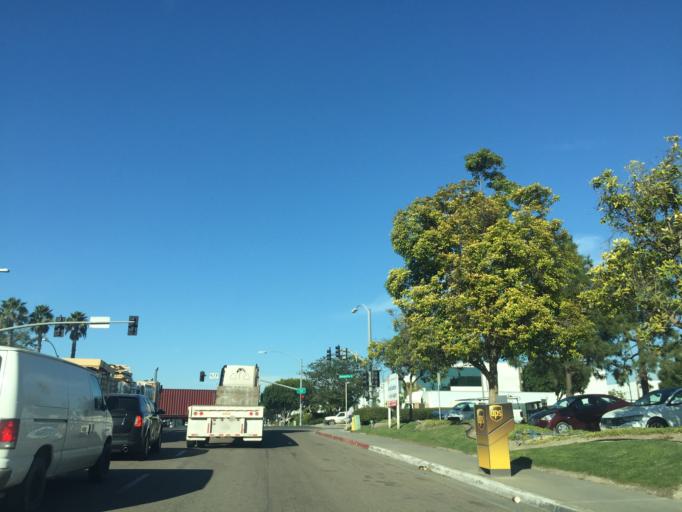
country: MX
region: Baja California
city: Tijuana
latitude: 32.5563
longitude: -116.9359
